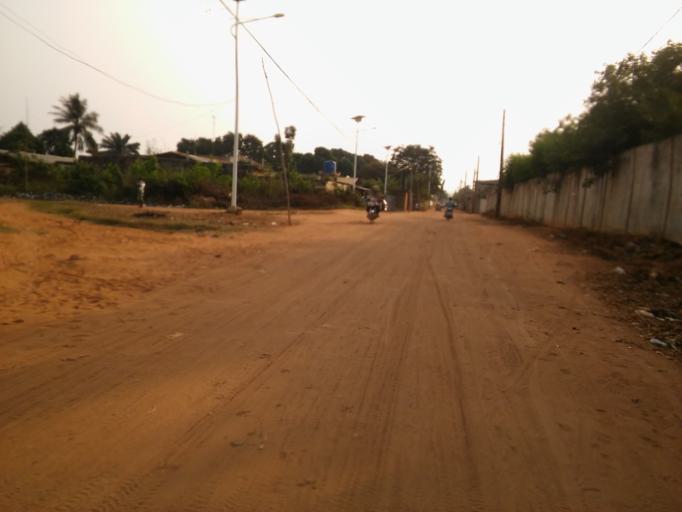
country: BJ
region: Atlantique
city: Abomey-Calavi
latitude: 6.4088
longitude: 2.3337
